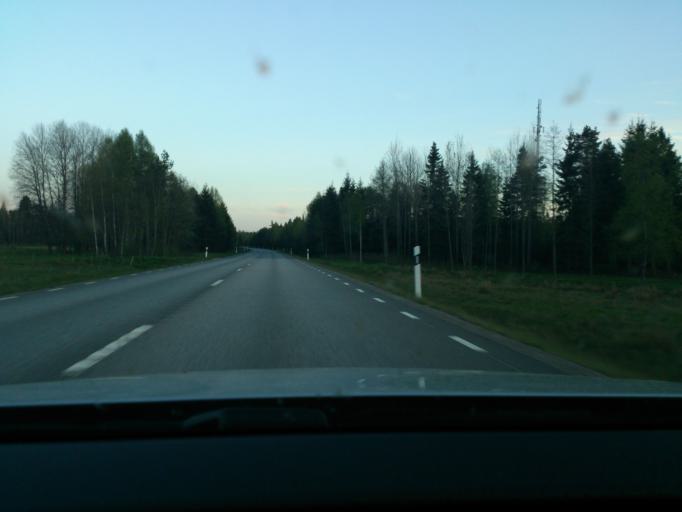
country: SE
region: Kronoberg
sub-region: Alvesta Kommun
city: Moheda
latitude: 57.0140
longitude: 14.5591
